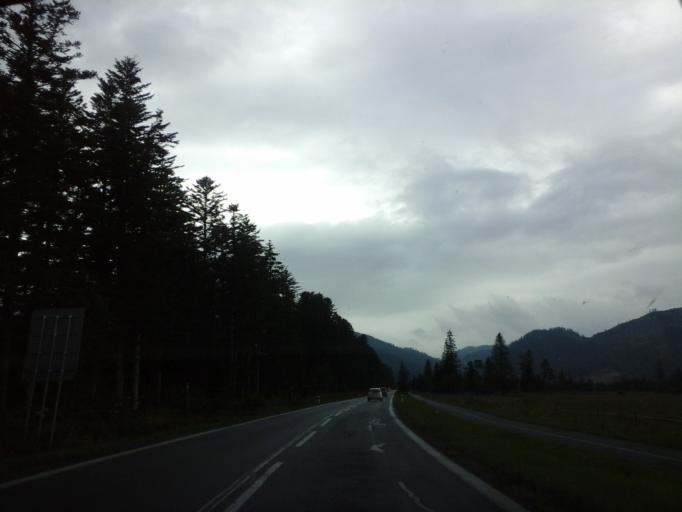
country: SK
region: Presovsky
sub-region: Okres Poprad
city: Zdiar
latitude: 49.2140
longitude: 20.3449
